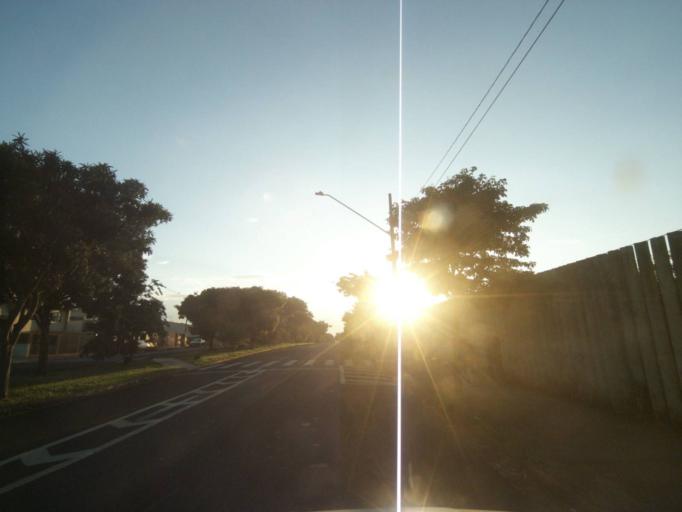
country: BR
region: Parana
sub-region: Londrina
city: Londrina
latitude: -23.3595
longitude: -51.1562
